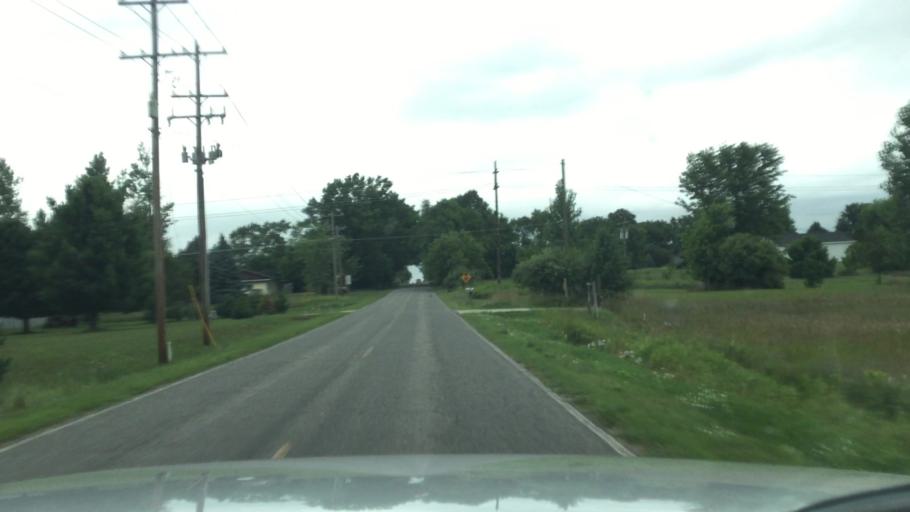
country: US
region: Michigan
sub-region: Montcalm County
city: Greenville
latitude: 43.1902
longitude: -85.2231
